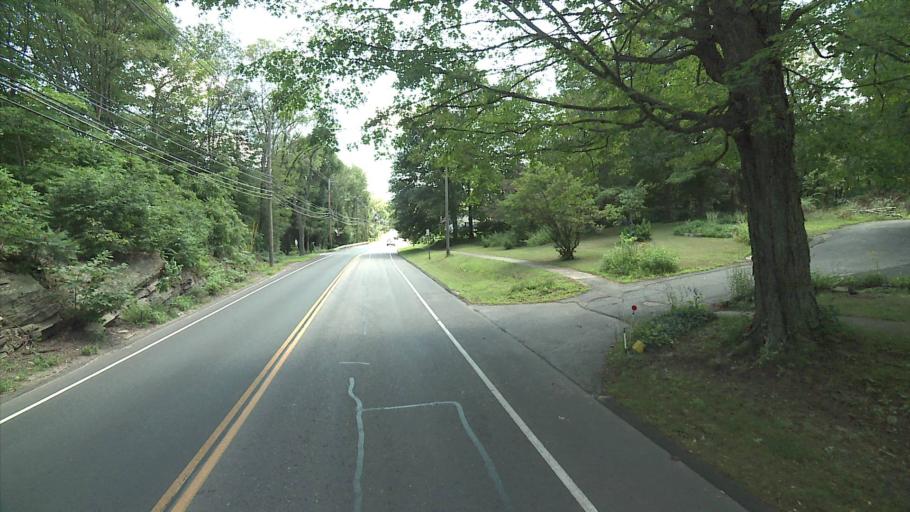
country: US
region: Connecticut
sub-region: Middlesex County
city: Deep River Center
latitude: 41.3760
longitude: -72.4316
